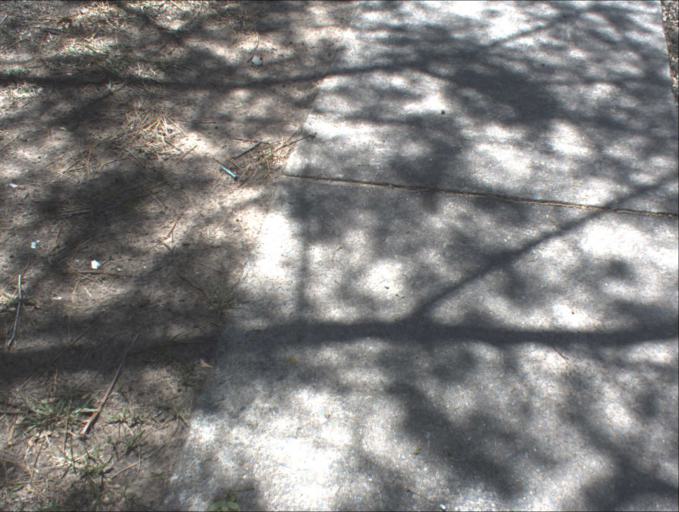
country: AU
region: Queensland
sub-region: Logan
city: Springwood
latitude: -27.6205
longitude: 153.1198
